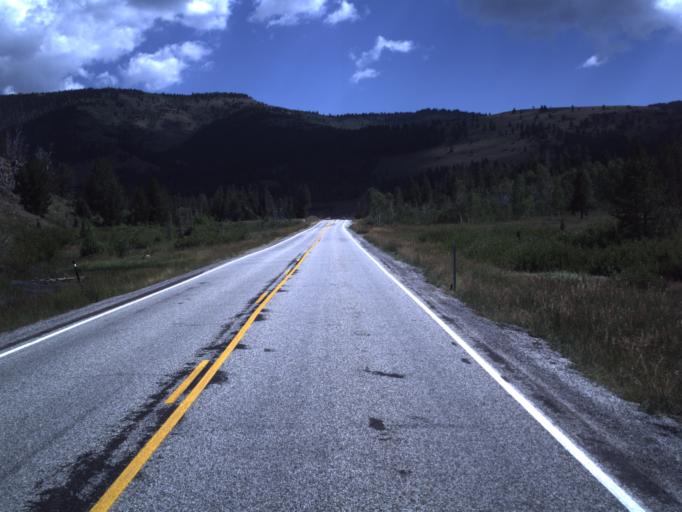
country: US
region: Utah
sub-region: Cache County
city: Richmond
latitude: 41.9598
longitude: -111.5366
